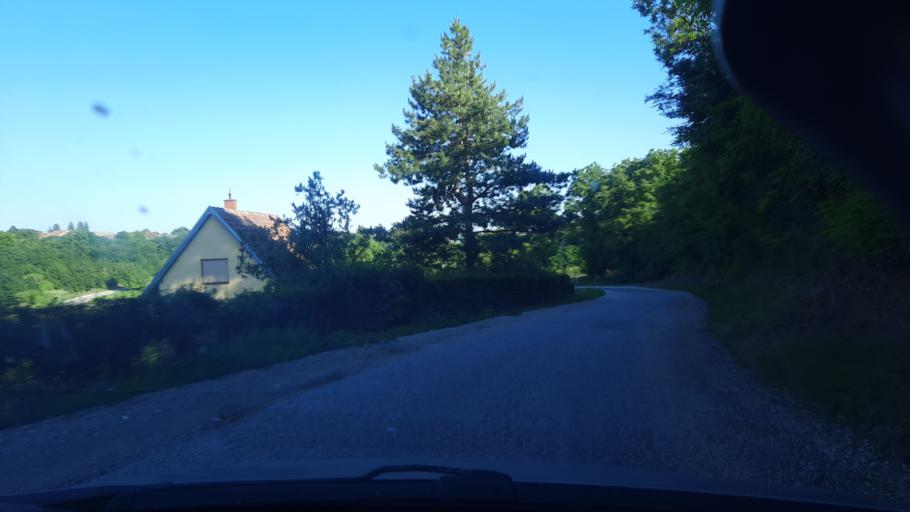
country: RS
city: Cortanovci
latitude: 45.1054
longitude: 19.9852
